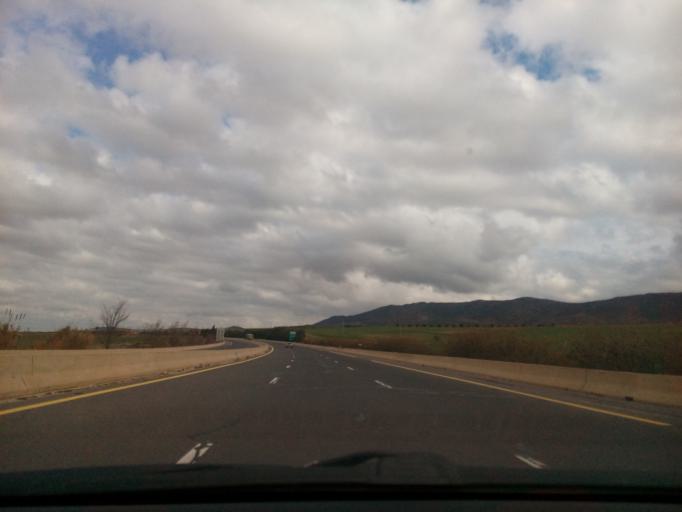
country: DZ
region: Tlemcen
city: Bensekrane
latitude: 34.9923
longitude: -1.2027
